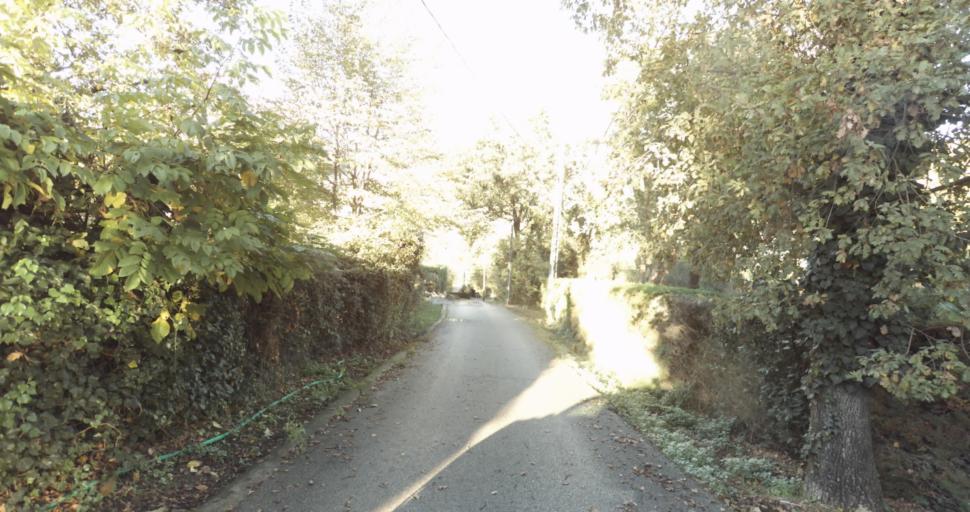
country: FR
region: Provence-Alpes-Cote d'Azur
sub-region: Departement des Alpes-Maritimes
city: La Gaude
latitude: 43.7176
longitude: 7.1376
